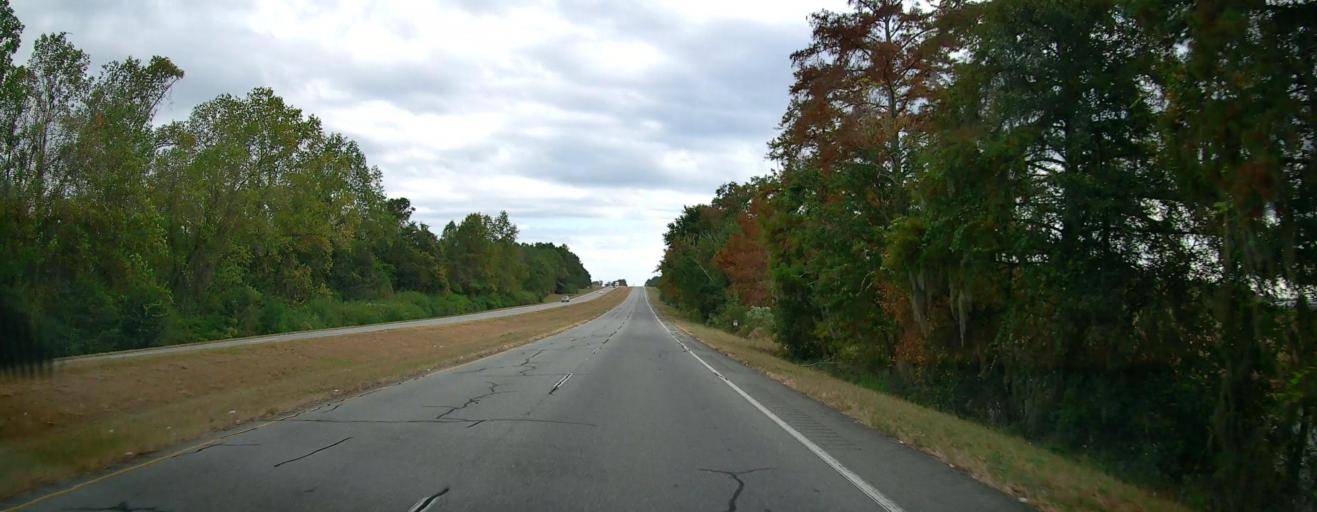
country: US
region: Georgia
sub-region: Thomas County
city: Meigs
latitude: 31.0947
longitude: -84.0950
